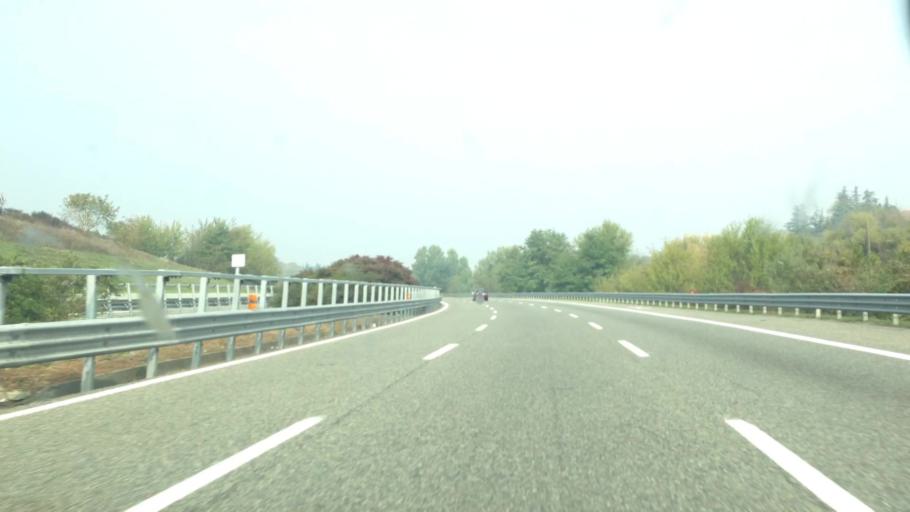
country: IT
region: Piedmont
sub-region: Provincia di Alessandria
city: San Salvatore Monferrato
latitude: 45.0001
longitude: 8.5404
